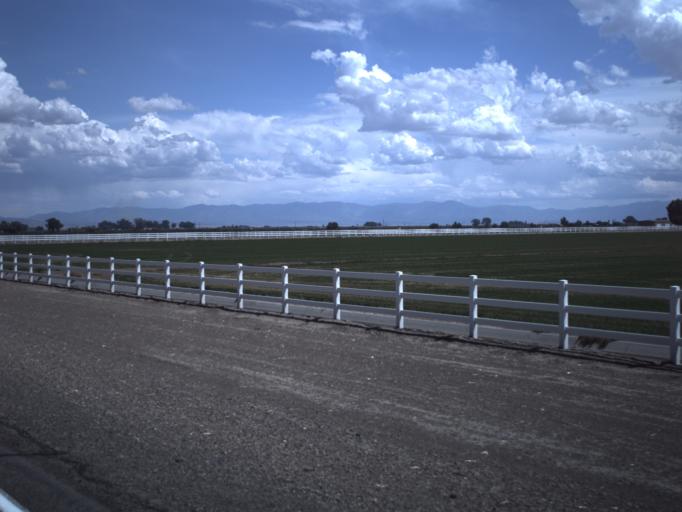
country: US
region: Utah
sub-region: Millard County
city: Delta
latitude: 39.3306
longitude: -112.6358
